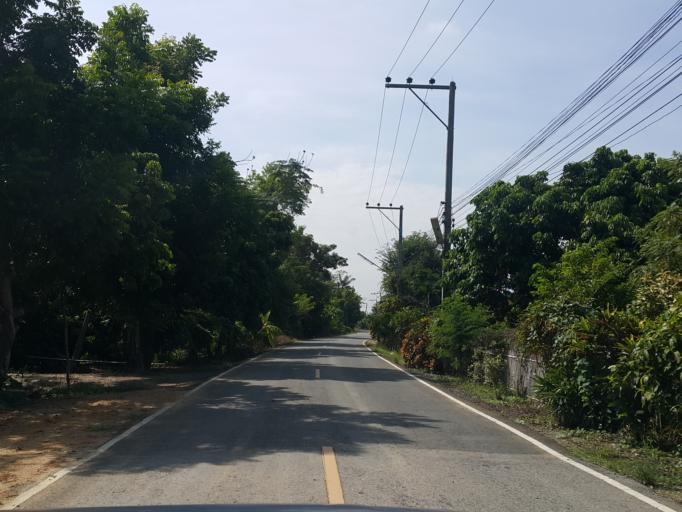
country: TH
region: Chiang Mai
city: Saraphi
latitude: 18.6869
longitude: 99.0749
